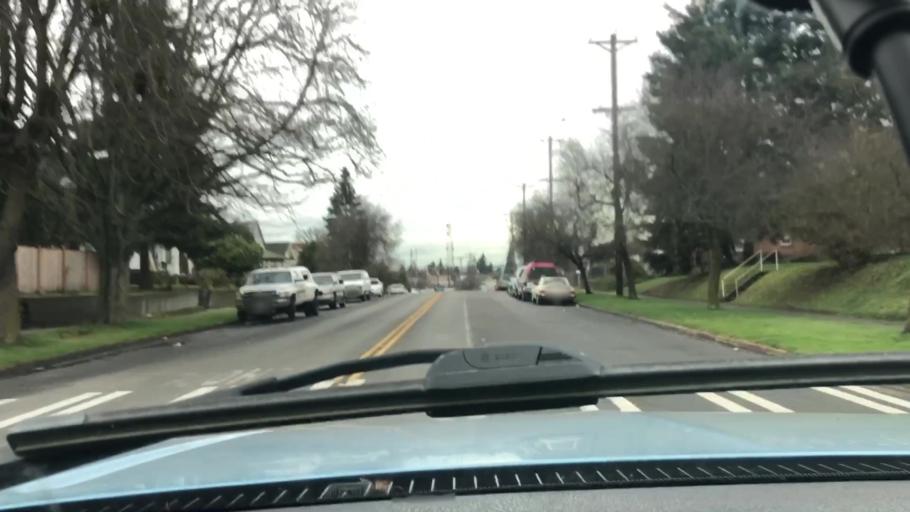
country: US
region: Washington
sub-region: Pierce County
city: Tacoma
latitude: 47.2265
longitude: -122.4208
